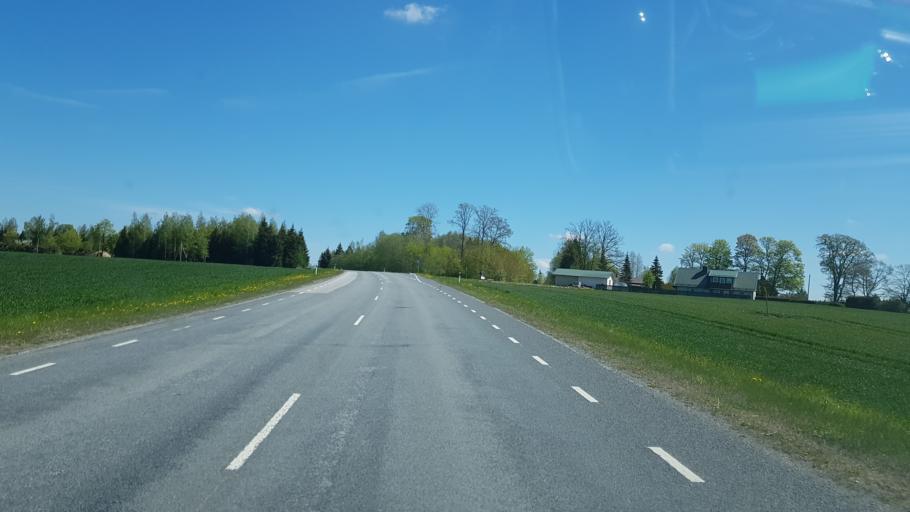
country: EE
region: Viljandimaa
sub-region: Viljandi linn
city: Viljandi
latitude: 58.3302
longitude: 25.6077
